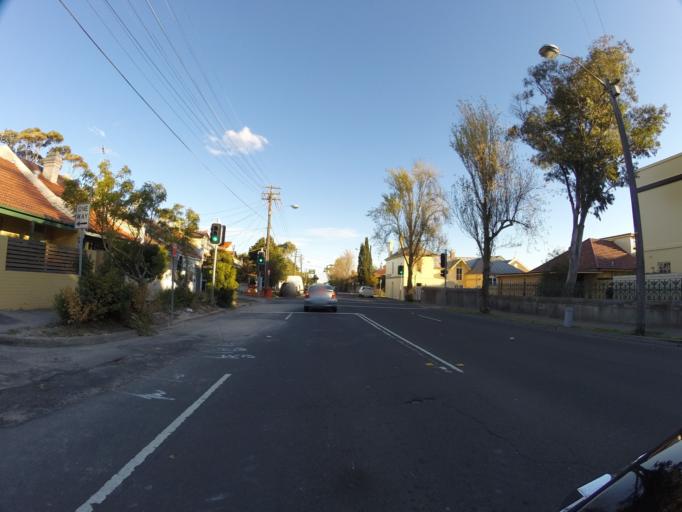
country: AU
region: New South Wales
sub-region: Waverley
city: Bondi Junction
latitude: -33.8976
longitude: 151.2542
